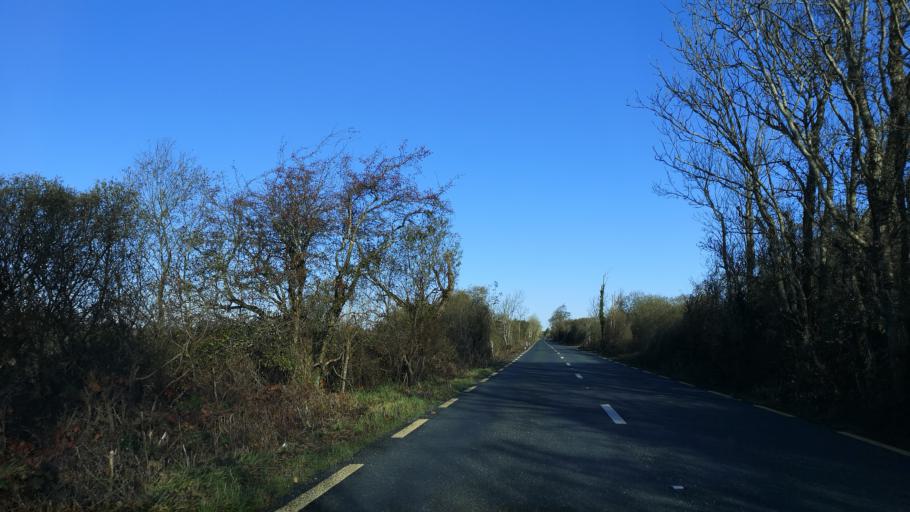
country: IE
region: Connaught
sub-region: County Galway
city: Claregalway
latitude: 53.3890
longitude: -9.0168
